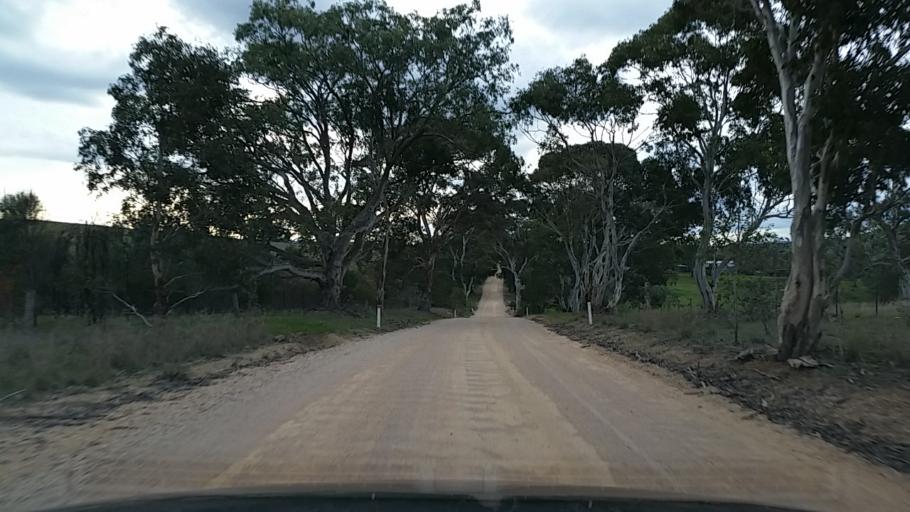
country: AU
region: South Australia
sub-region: Mount Barker
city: Nairne
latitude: -34.9710
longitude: 139.0285
